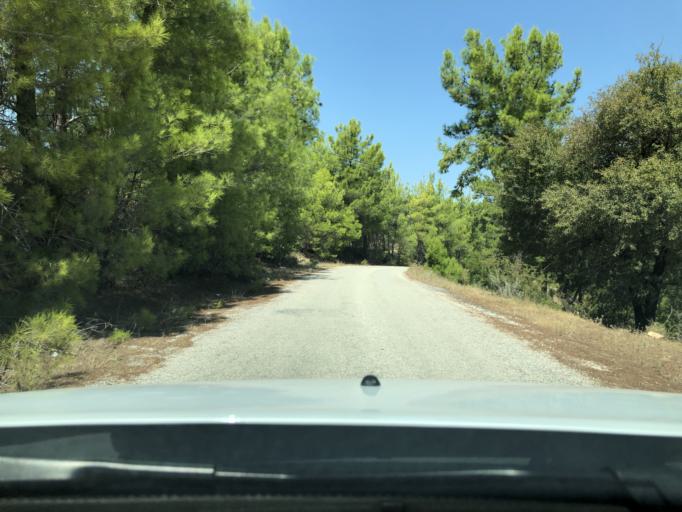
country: TR
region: Antalya
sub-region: Manavgat
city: Manavgat
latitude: 36.8381
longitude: 31.5338
